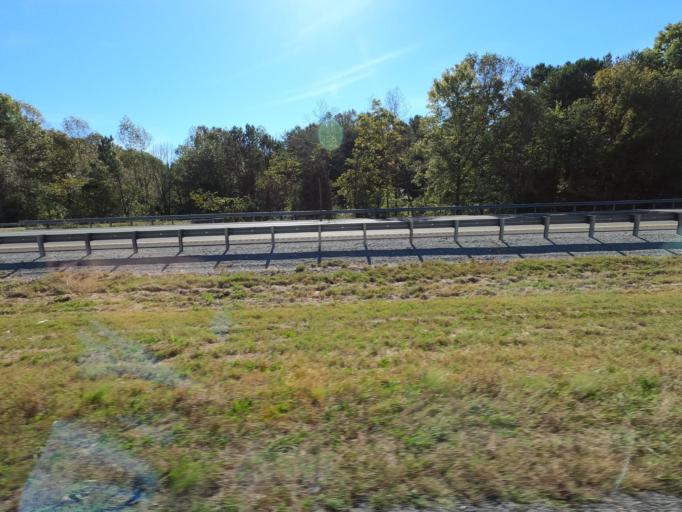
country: US
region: Tennessee
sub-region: Williamson County
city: Fairview
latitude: 36.0293
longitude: -87.1741
